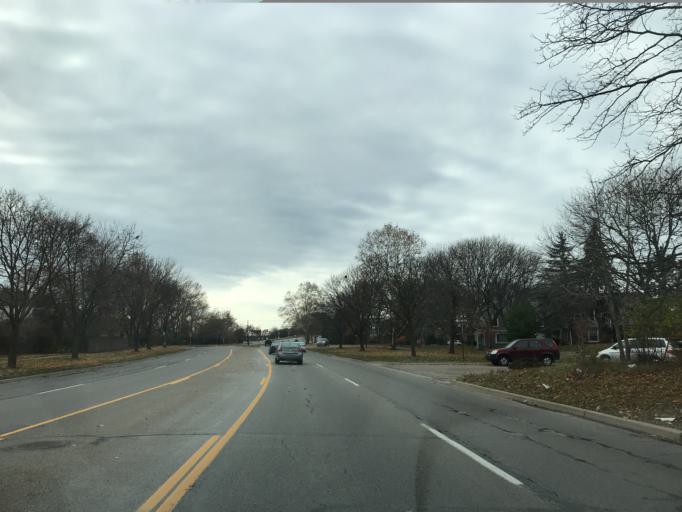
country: US
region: Michigan
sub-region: Washtenaw County
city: Ann Arbor
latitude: 42.2451
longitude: -83.7261
